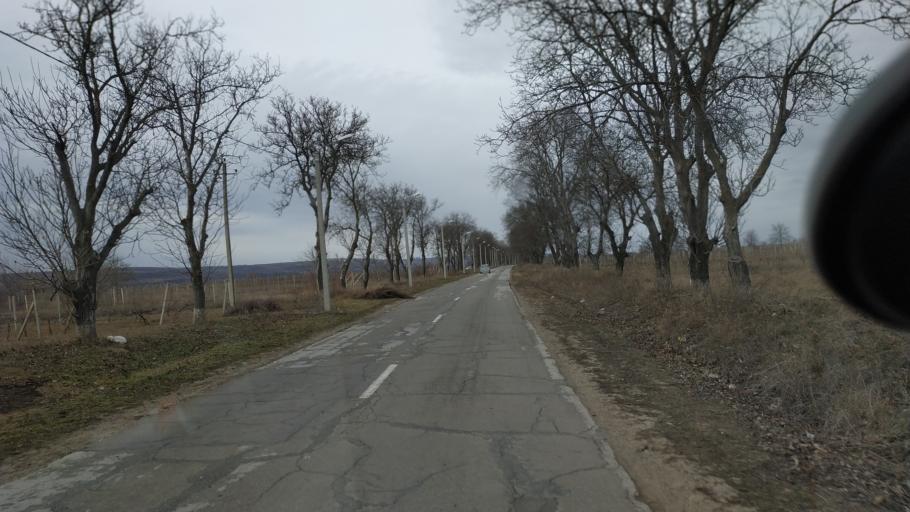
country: MD
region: Telenesti
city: Cocieri
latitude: 47.3187
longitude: 29.1017
